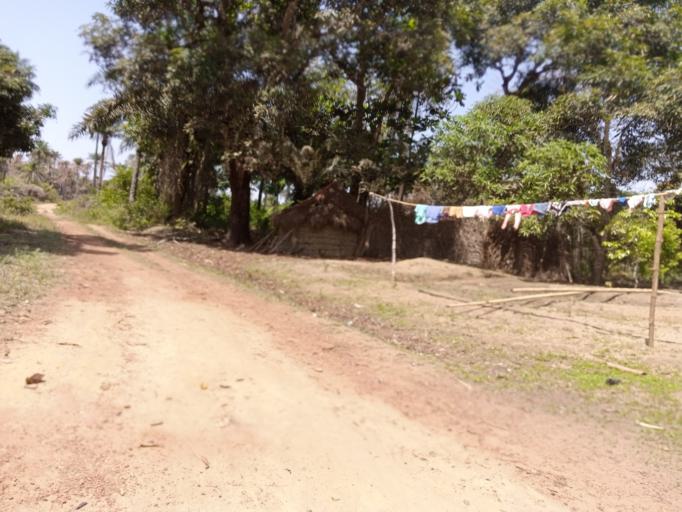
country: SL
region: Western Area
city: Waterloo
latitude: 8.2988
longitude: -13.0109
